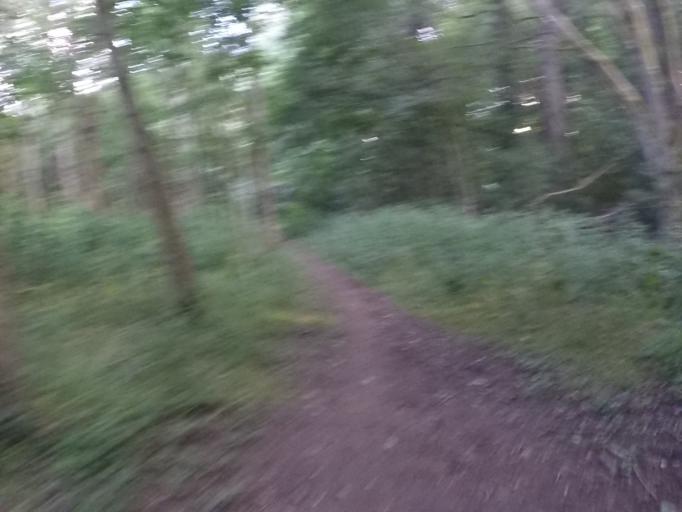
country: GB
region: England
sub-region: Oxfordshire
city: Charlbury
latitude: 51.9006
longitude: -1.4992
